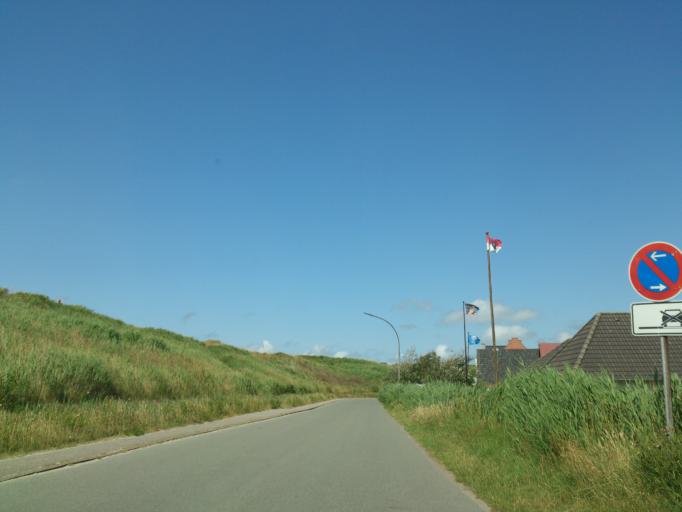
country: DE
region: Schleswig-Holstein
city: Sankt Peter-Ording
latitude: 54.3392
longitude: 8.6022
